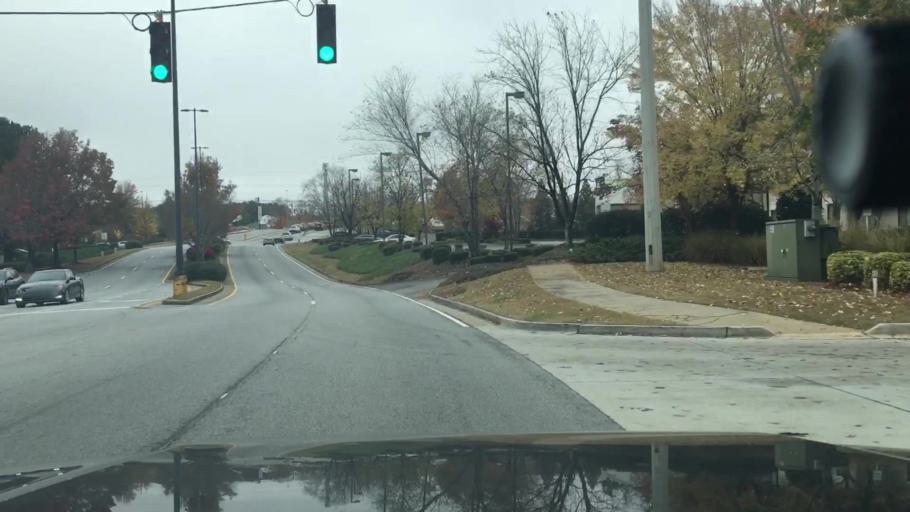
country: US
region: Georgia
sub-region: Coweta County
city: East Newnan
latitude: 33.3946
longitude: -84.7418
